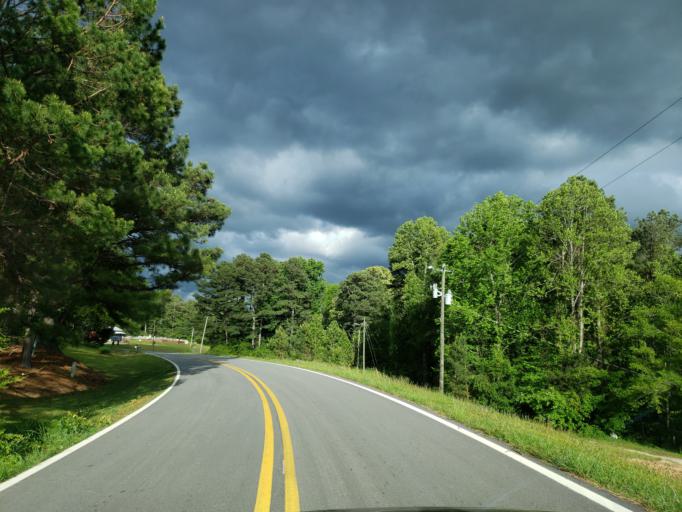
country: US
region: Georgia
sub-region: Haralson County
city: Tallapoosa
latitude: 33.8627
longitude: -85.3451
